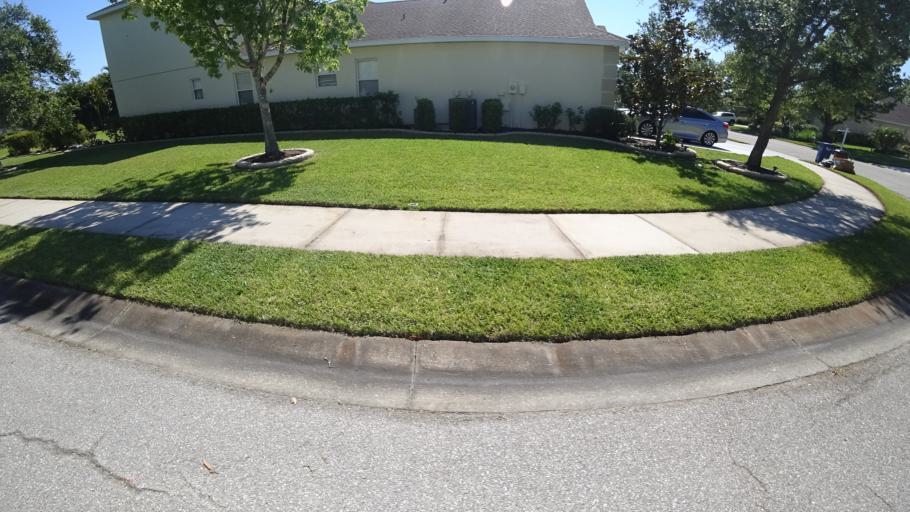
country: US
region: Florida
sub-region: Manatee County
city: Ellenton
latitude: 27.5667
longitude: -82.4444
